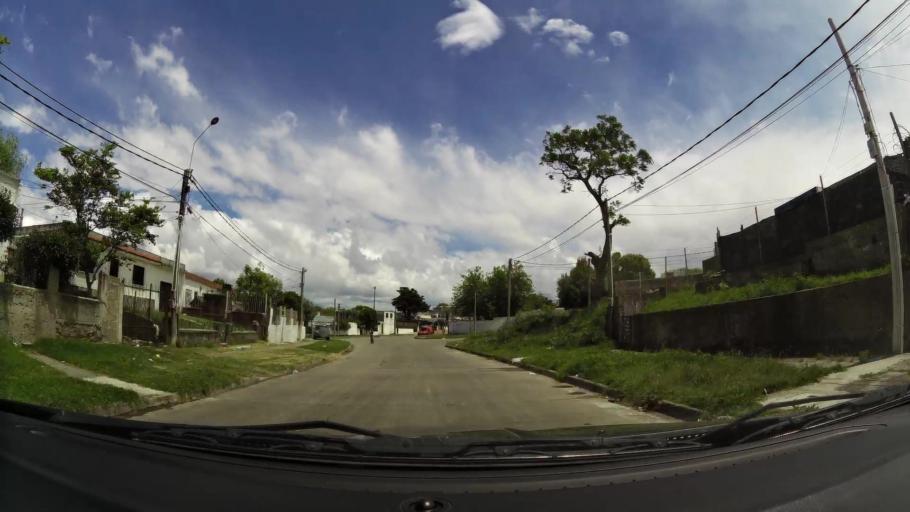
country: UY
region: Montevideo
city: Montevideo
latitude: -34.8804
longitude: -56.1258
